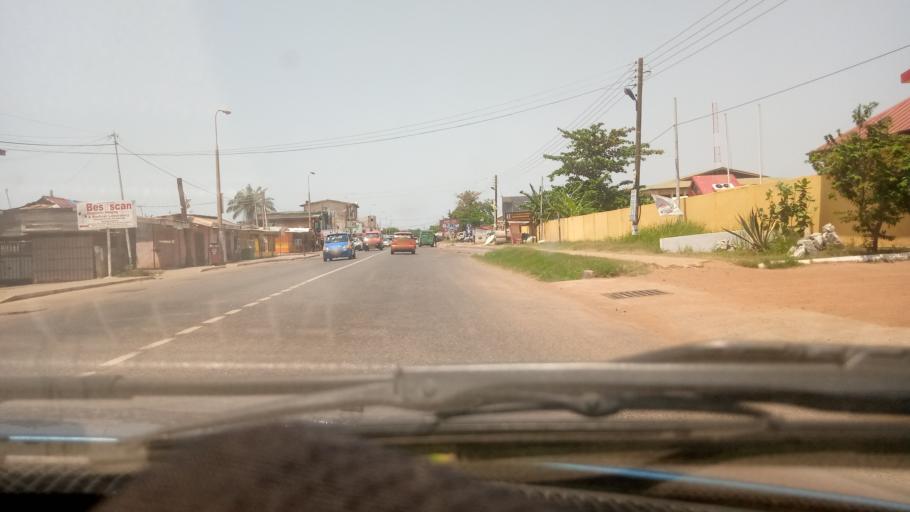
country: GH
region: Greater Accra
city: Accra
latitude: 5.5350
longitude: -0.2323
